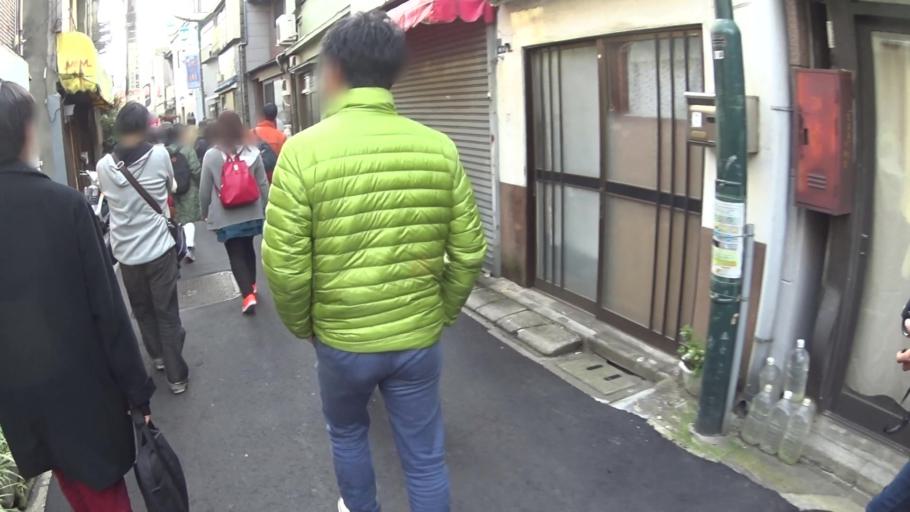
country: JP
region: Tokyo
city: Urayasu
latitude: 35.7211
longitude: 139.8118
